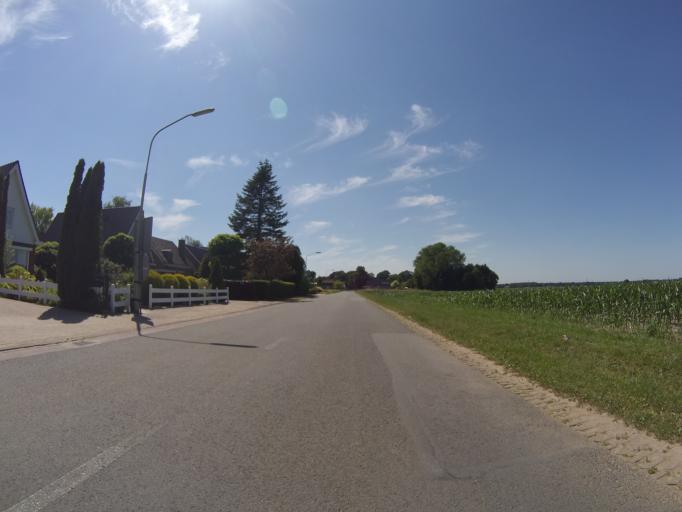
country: NL
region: Drenthe
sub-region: Gemeente Emmen
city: Emmen
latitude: 52.7855
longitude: 6.8847
